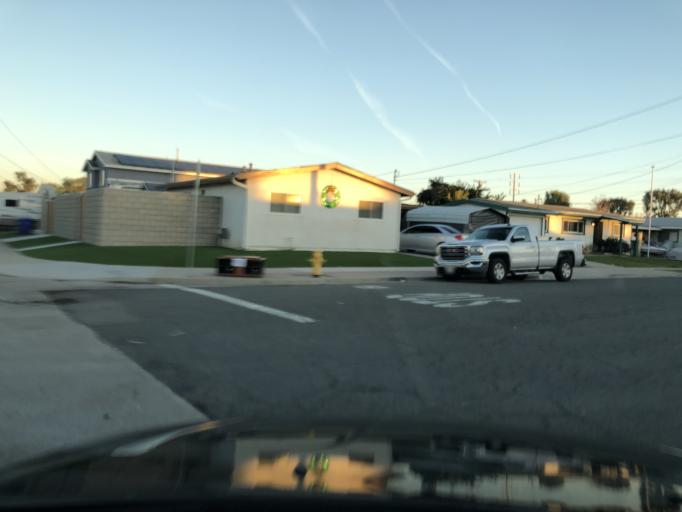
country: US
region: California
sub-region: San Diego County
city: La Jolla
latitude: 32.8359
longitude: -117.1753
